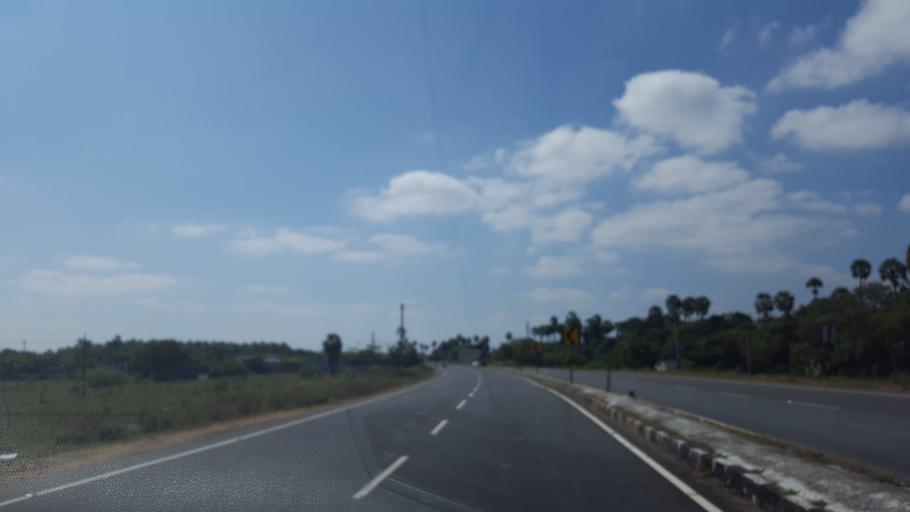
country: IN
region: Tamil Nadu
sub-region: Kancheepuram
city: Mamallapuram
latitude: 12.6216
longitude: 80.1700
